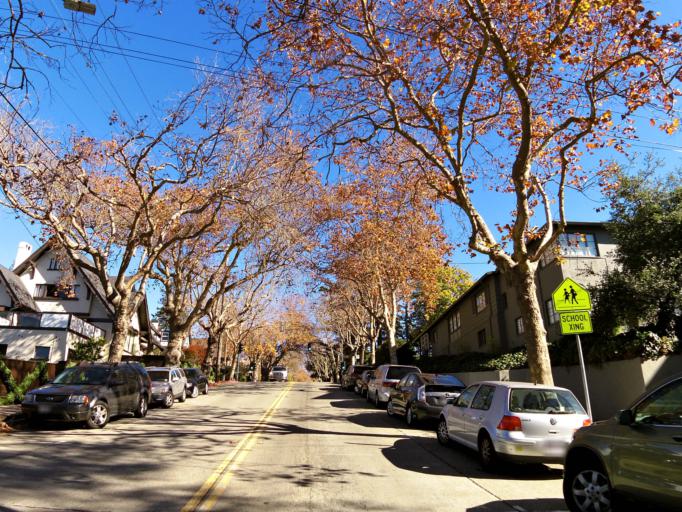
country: US
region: California
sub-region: Alameda County
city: Piedmont
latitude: 37.8251
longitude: -122.2364
